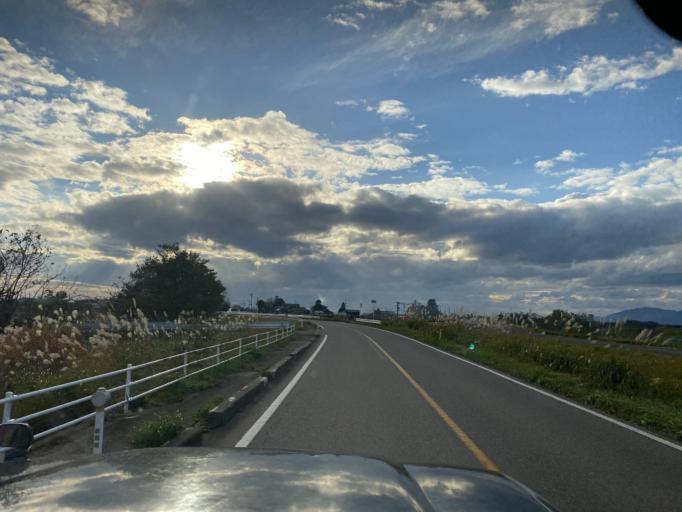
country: JP
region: Niigata
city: Kamo
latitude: 37.6837
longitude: 139.0232
